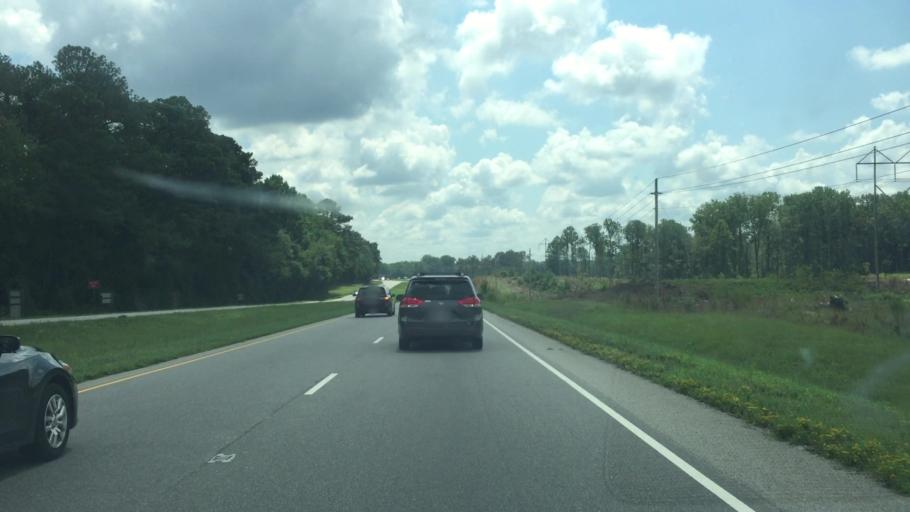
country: US
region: North Carolina
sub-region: Scotland County
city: Laurel Hill
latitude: 34.8202
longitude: -79.5786
